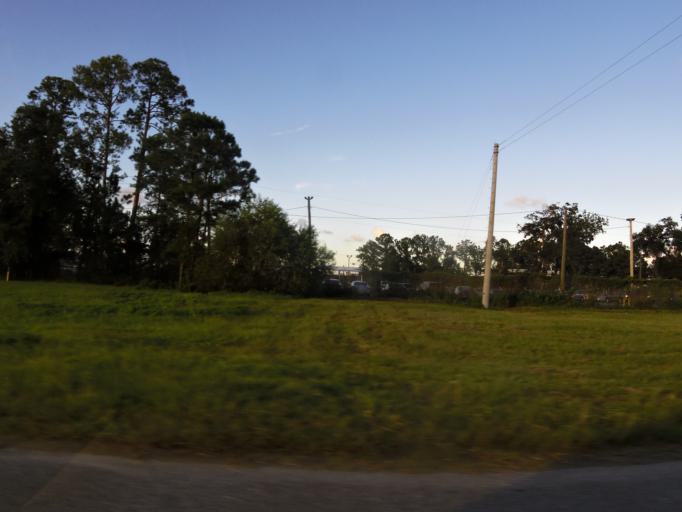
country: US
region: Georgia
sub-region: Glynn County
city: Brunswick
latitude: 31.1184
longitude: -81.5404
